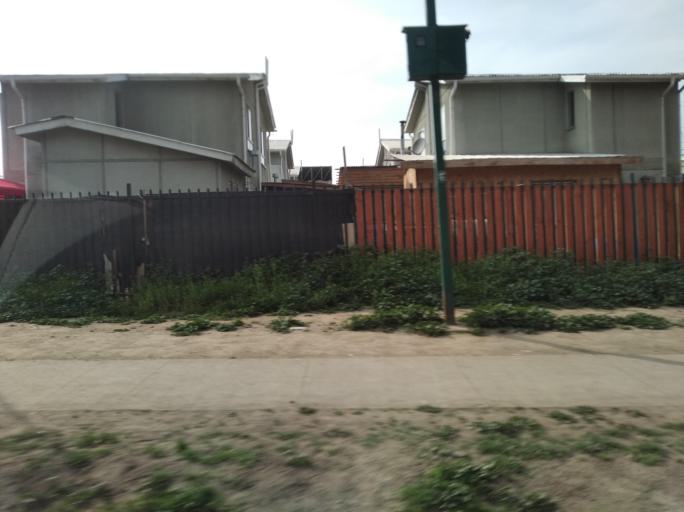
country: CL
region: Santiago Metropolitan
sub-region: Provincia de Chacabuco
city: Lampa
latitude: -33.2783
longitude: -70.8889
